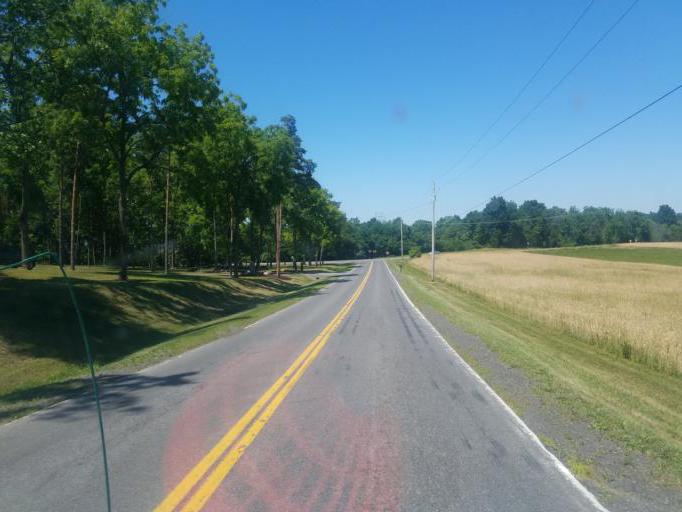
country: US
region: New York
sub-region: Yates County
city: Penn Yan
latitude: 42.7512
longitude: -77.0031
